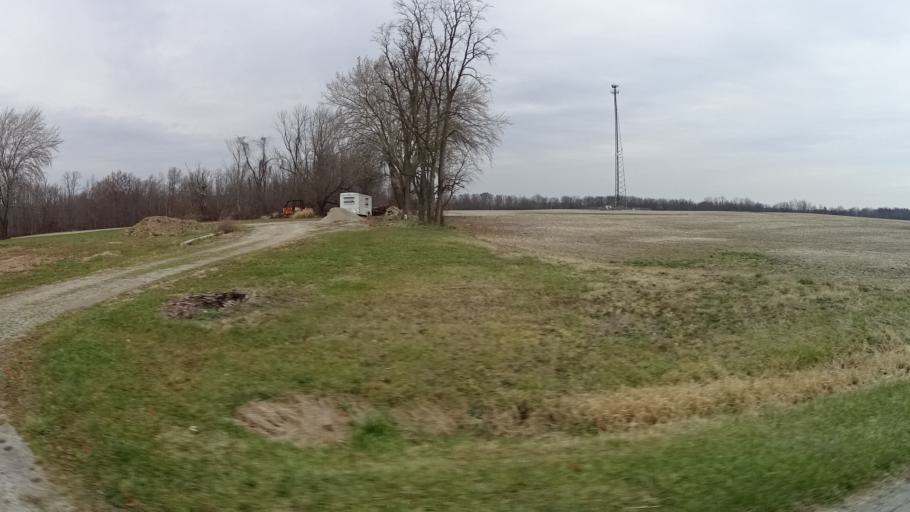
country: US
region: Ohio
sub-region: Lorain County
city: Lagrange
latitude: 41.1542
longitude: -82.1327
